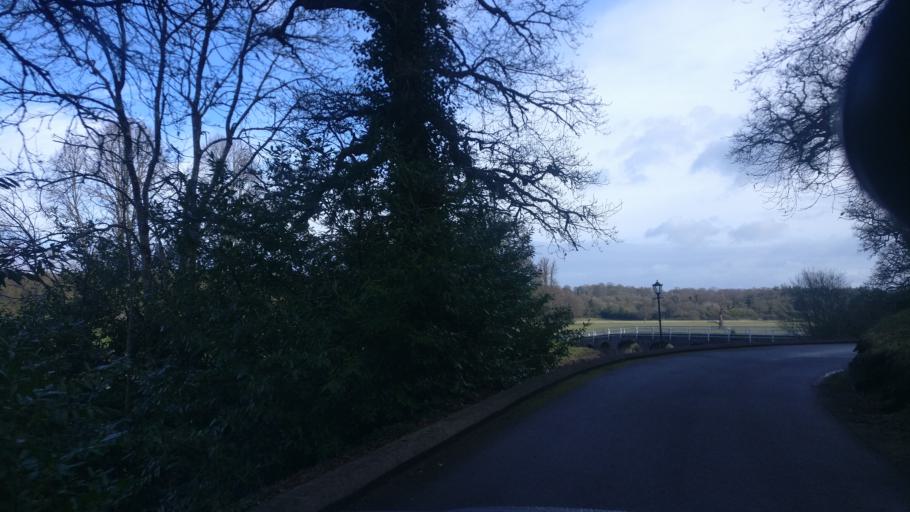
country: IE
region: Leinster
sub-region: Kilkenny
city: Thomastown
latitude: 52.5319
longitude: -7.1908
